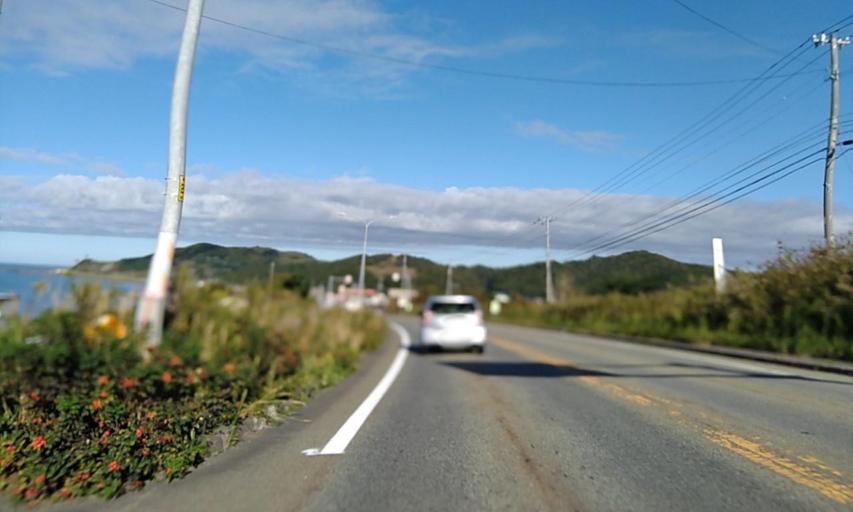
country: JP
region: Hokkaido
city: Shizunai-furukawacho
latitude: 42.1837
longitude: 142.7273
